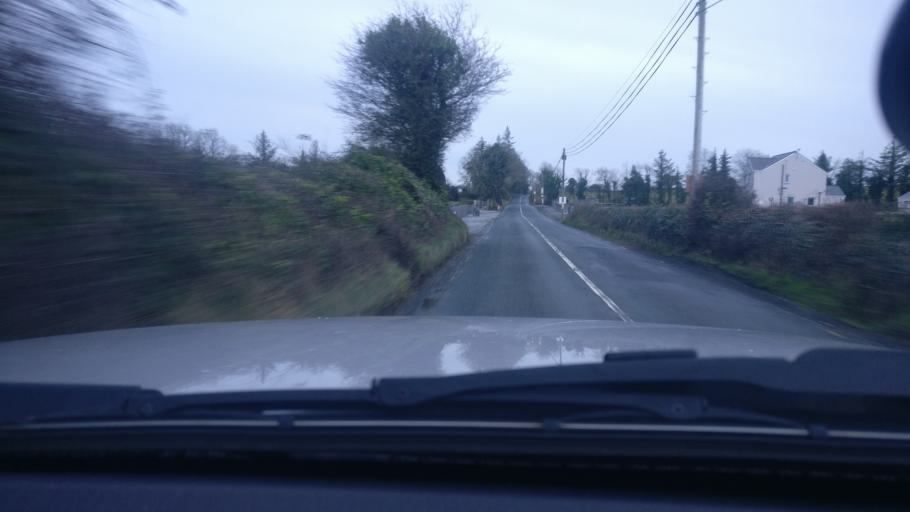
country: IE
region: Connaught
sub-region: County Galway
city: Loughrea
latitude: 53.1686
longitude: -8.5224
